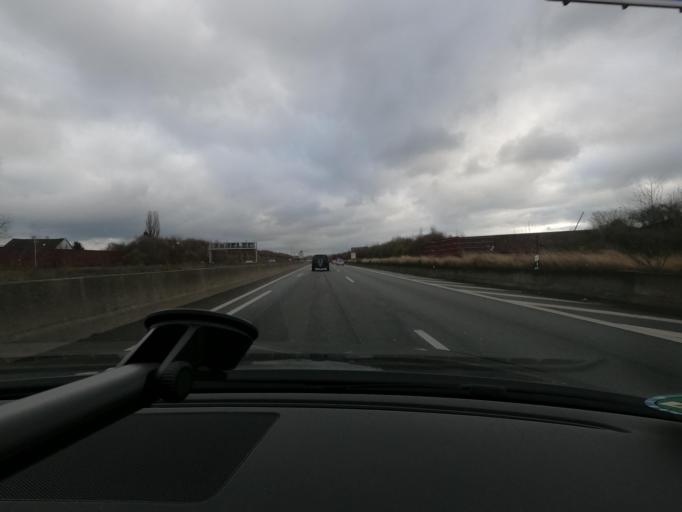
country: DE
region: North Rhine-Westphalia
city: Witten
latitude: 51.4974
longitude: 7.3881
